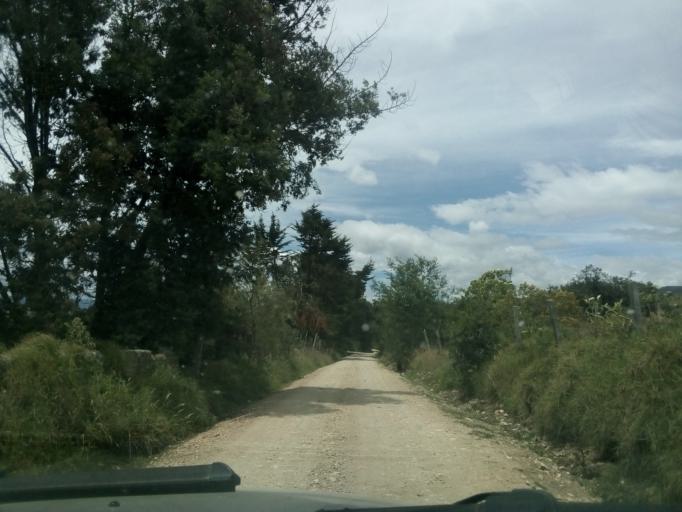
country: CO
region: Boyaca
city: Toca
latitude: 5.6032
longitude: -73.1532
